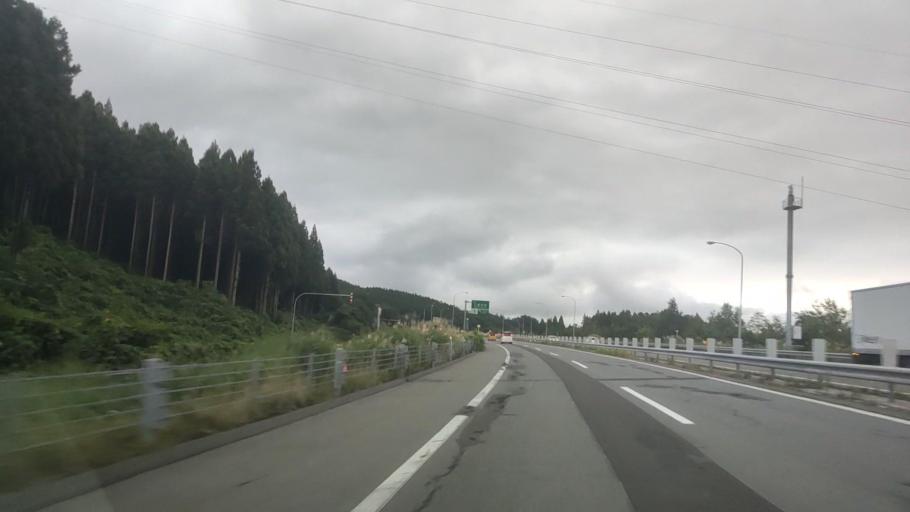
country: JP
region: Hokkaido
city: Nanae
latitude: 41.9020
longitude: 140.7004
